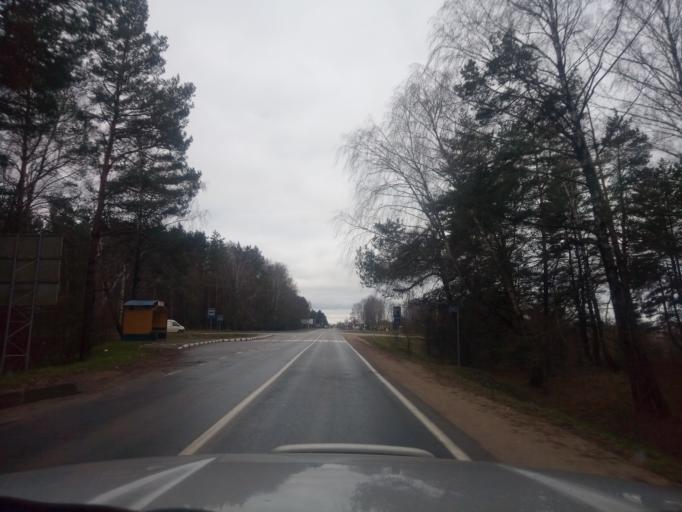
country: BY
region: Minsk
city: Kapyl'
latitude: 53.1575
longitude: 27.1050
